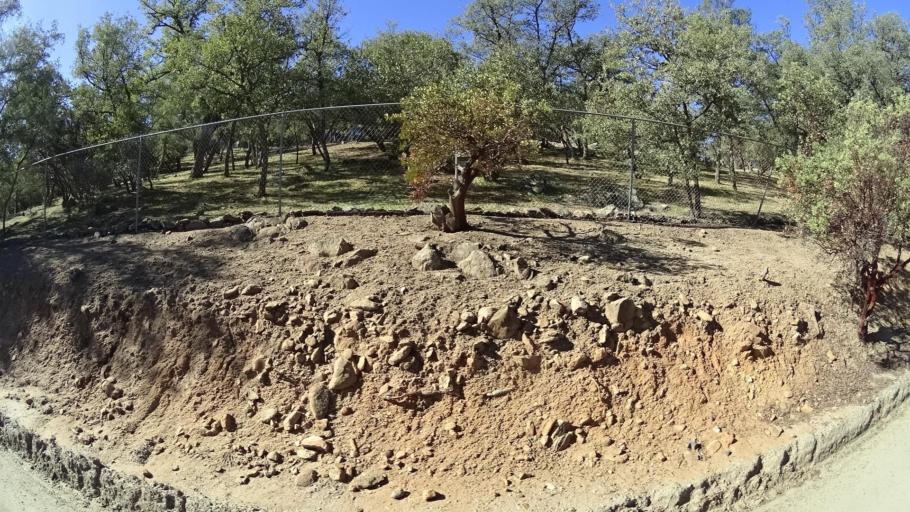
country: US
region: California
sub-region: San Diego County
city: Descanso
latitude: 32.8668
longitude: -116.6471
